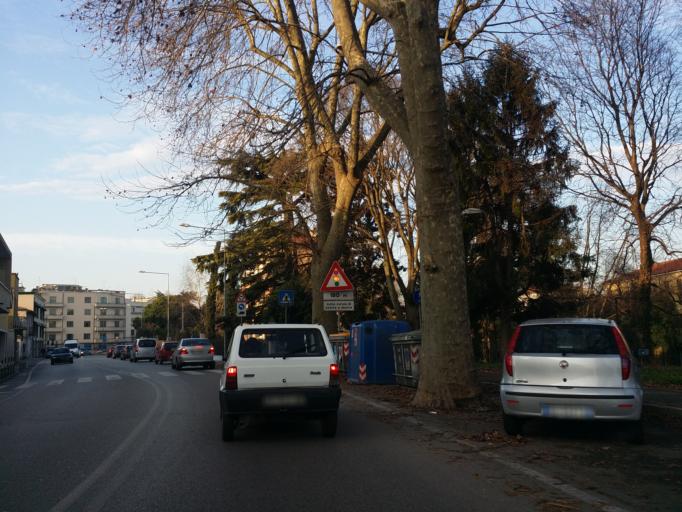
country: IT
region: Veneto
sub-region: Provincia di Padova
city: Padova
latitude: 45.4024
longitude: 11.8637
